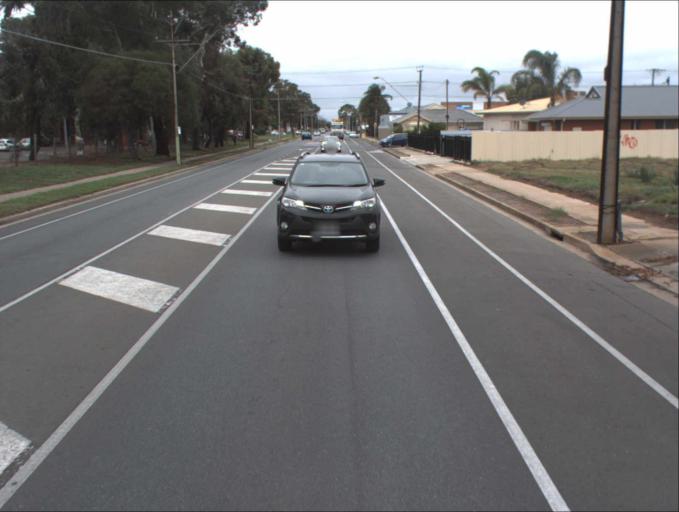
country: AU
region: South Australia
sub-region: Charles Sturt
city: Woodville
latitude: -34.8696
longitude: 138.5659
